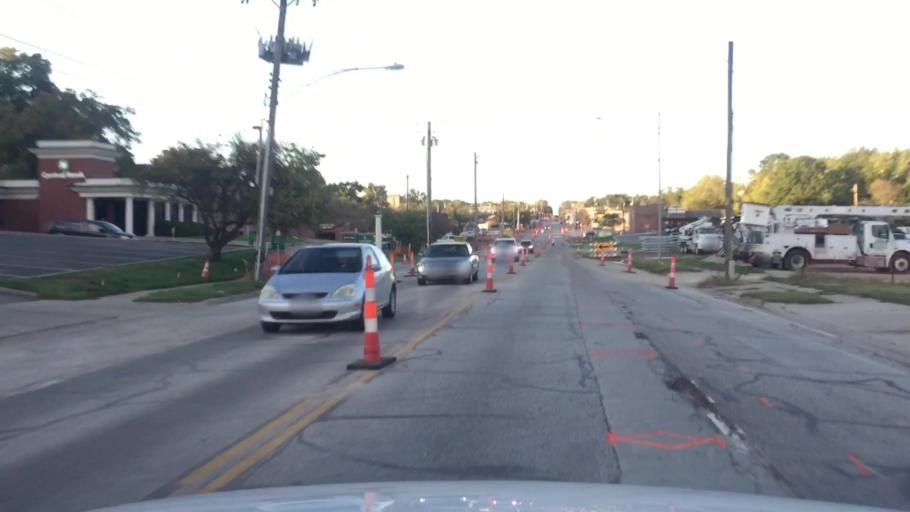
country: US
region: Kansas
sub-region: Johnson County
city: Merriam
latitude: 39.0174
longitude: -94.7146
